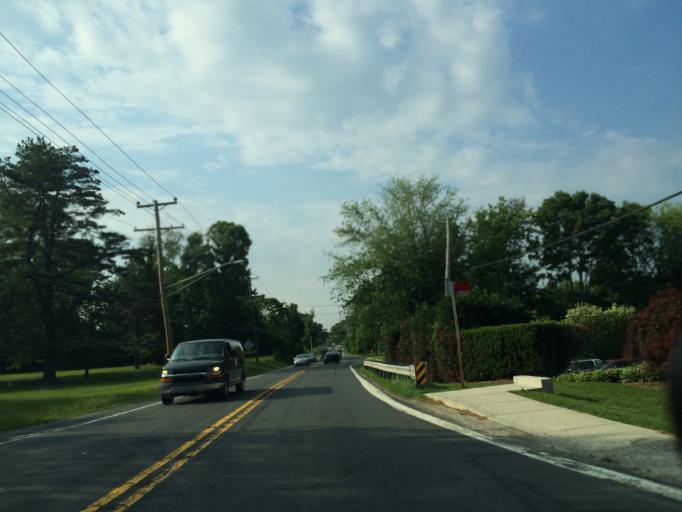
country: US
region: Maryland
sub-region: Montgomery County
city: Ashton-Sandy Spring
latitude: 39.1398
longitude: -76.9960
